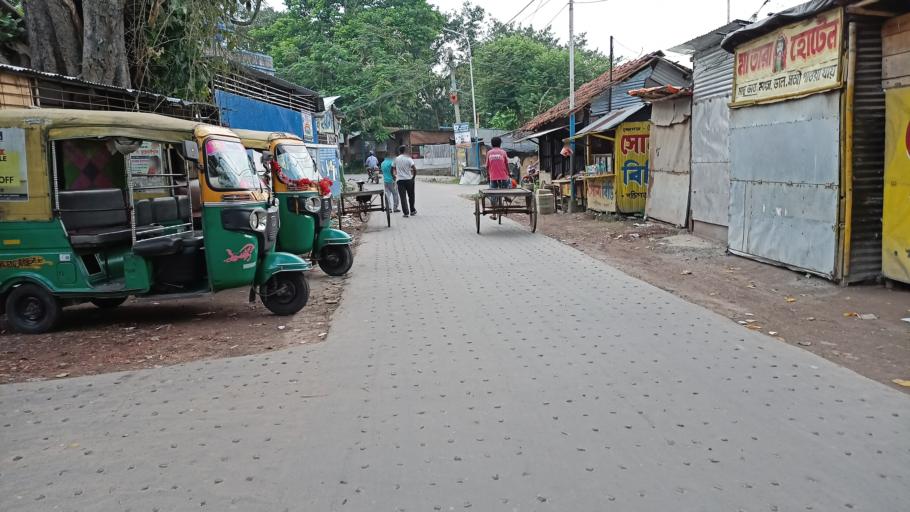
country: IN
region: West Bengal
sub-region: North 24 Parganas
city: Bangaon
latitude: 23.0461
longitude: 88.8276
